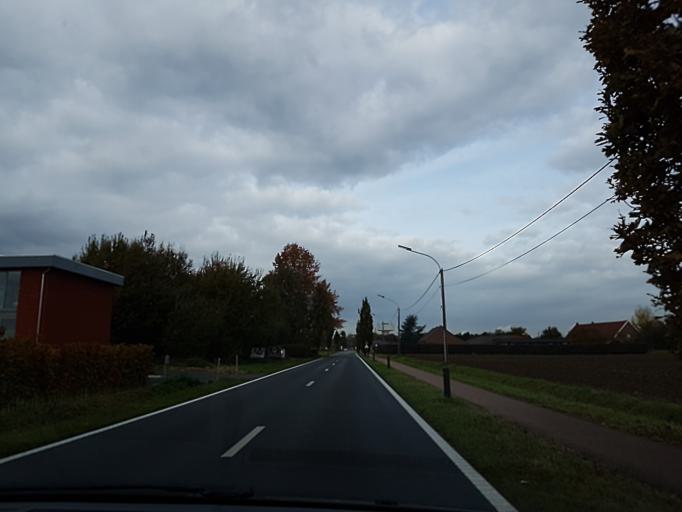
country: BE
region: Flanders
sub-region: Provincie Antwerpen
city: Ranst
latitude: 51.1767
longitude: 4.5619
